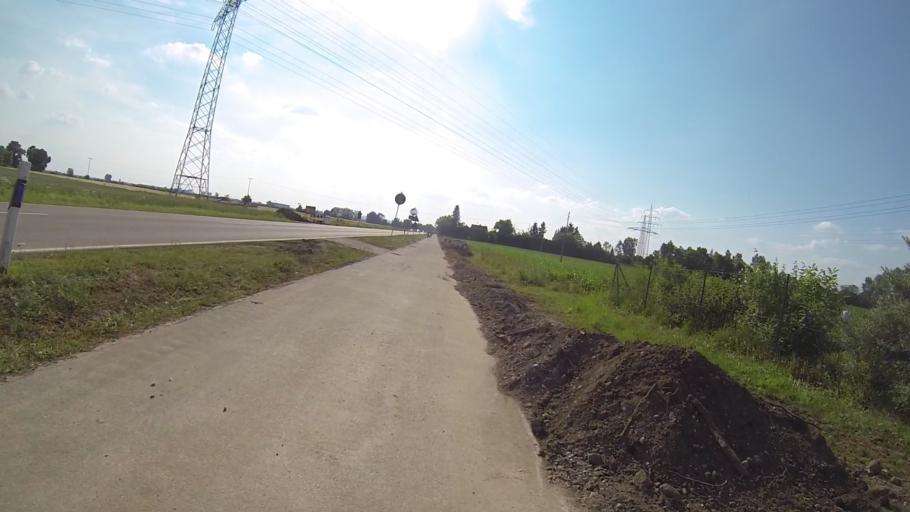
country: DE
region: Bavaria
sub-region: Swabia
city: Holzheim
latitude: 48.3873
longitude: 10.0590
